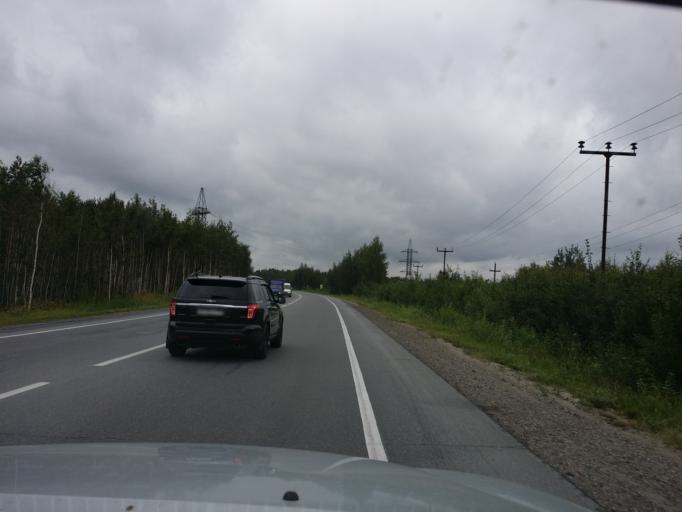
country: RU
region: Khanty-Mansiyskiy Avtonomnyy Okrug
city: Nizhnevartovsk
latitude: 61.0285
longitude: 76.3636
